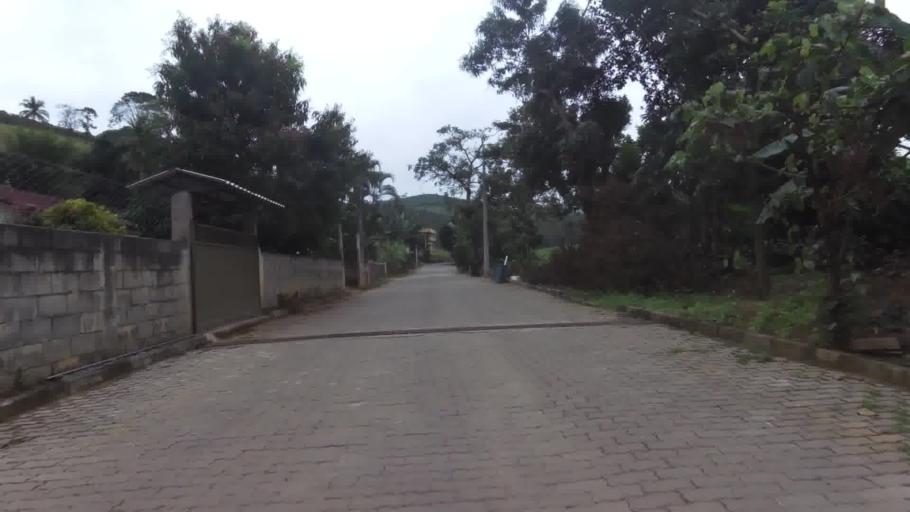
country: BR
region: Espirito Santo
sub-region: Iconha
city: Iconha
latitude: -20.7805
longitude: -40.8282
